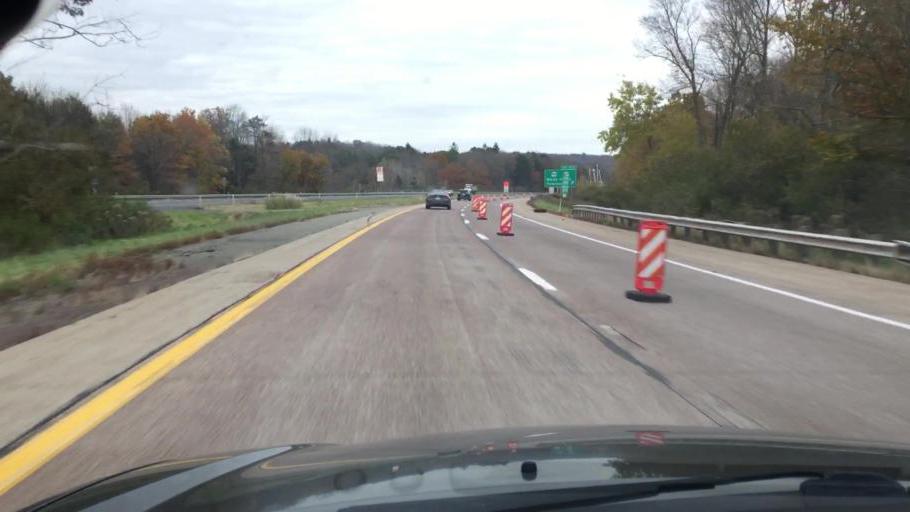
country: US
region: Pennsylvania
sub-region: Luzerne County
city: White Haven
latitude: 41.0571
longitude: -75.7865
